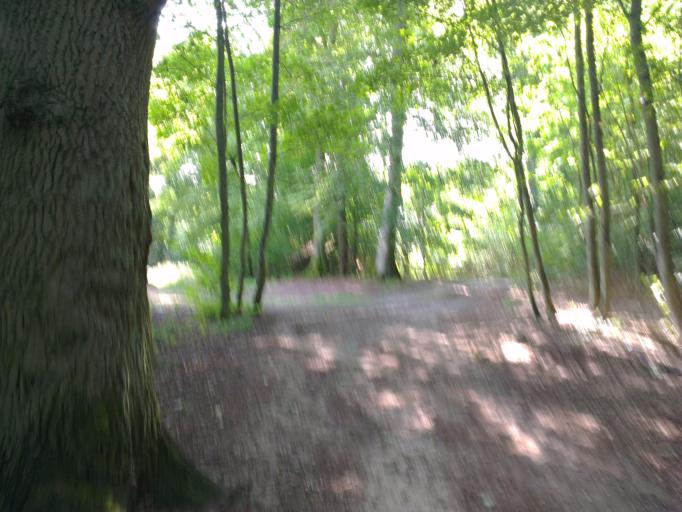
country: DK
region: Capital Region
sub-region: Frederikssund Kommune
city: Frederikssund
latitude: 55.8424
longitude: 12.0285
